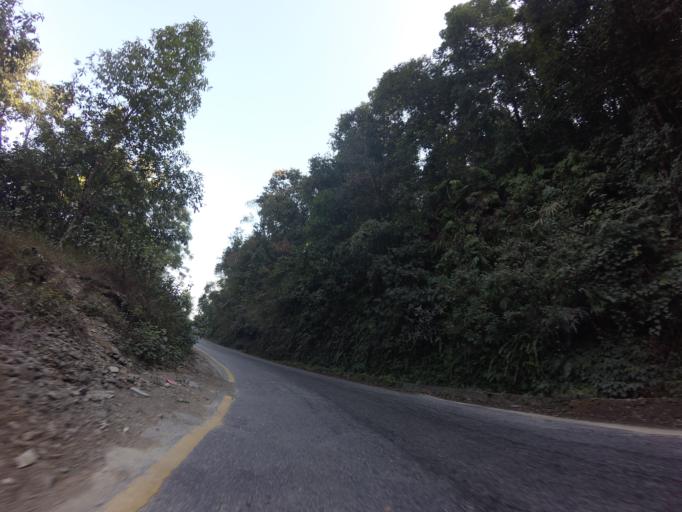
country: NP
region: Western Region
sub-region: Gandaki Zone
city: Pokhara
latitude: 28.1910
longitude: 83.8996
